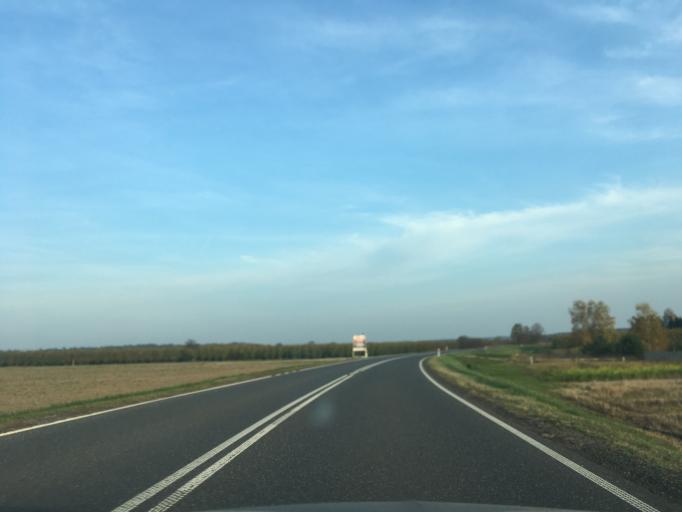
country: PL
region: Lodz Voivodeship
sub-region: Powiat skierniewicki
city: Kowiesy
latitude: 51.9239
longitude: 20.4226
